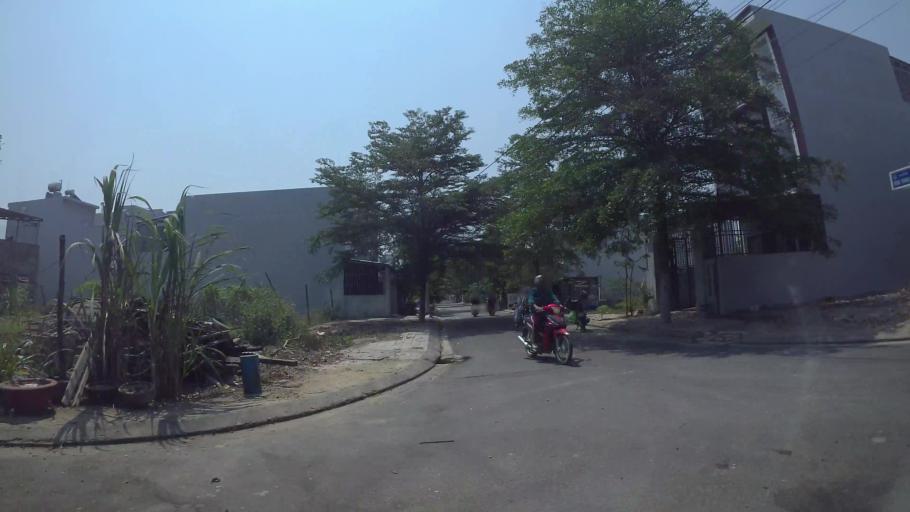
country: VN
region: Da Nang
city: Ngu Hanh Son
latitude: 15.9869
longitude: 108.2588
